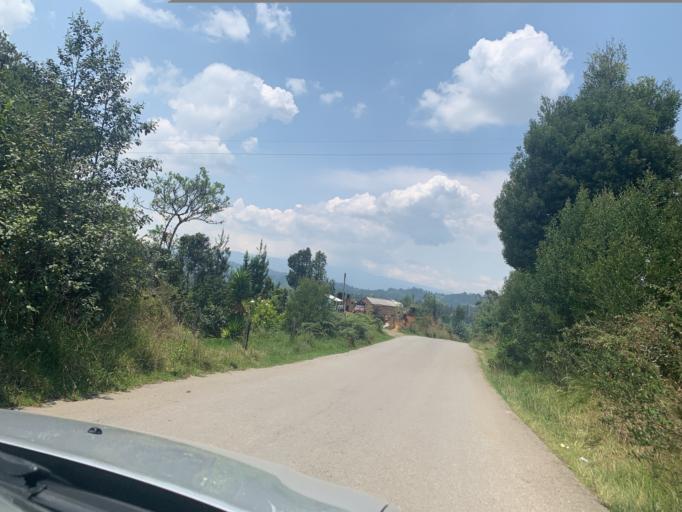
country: CO
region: Boyaca
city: Chiquinquira
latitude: 5.5618
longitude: -73.7510
